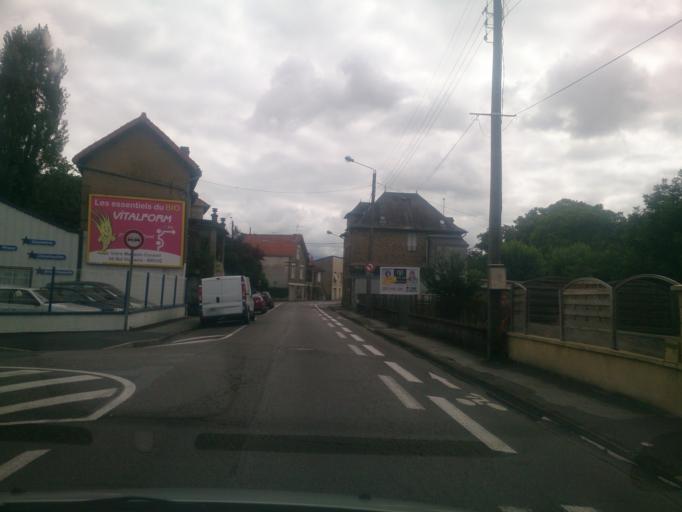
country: FR
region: Limousin
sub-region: Departement de la Correze
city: Brive-la-Gaillarde
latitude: 45.1648
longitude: 1.5267
